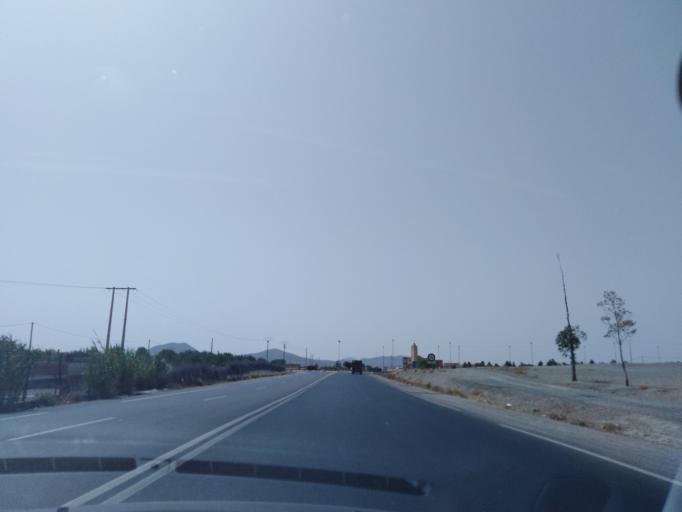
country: MA
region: Marrakech-Tensift-Al Haouz
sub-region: Marrakech
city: Marrakesh
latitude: 31.7724
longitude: -8.1291
